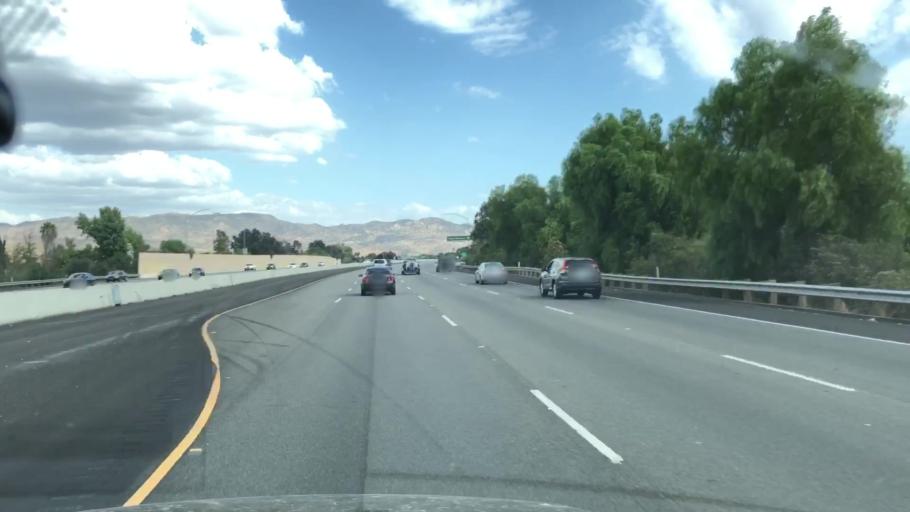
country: US
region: California
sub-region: Ventura County
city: Santa Susana
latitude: 34.2822
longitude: -118.7242
